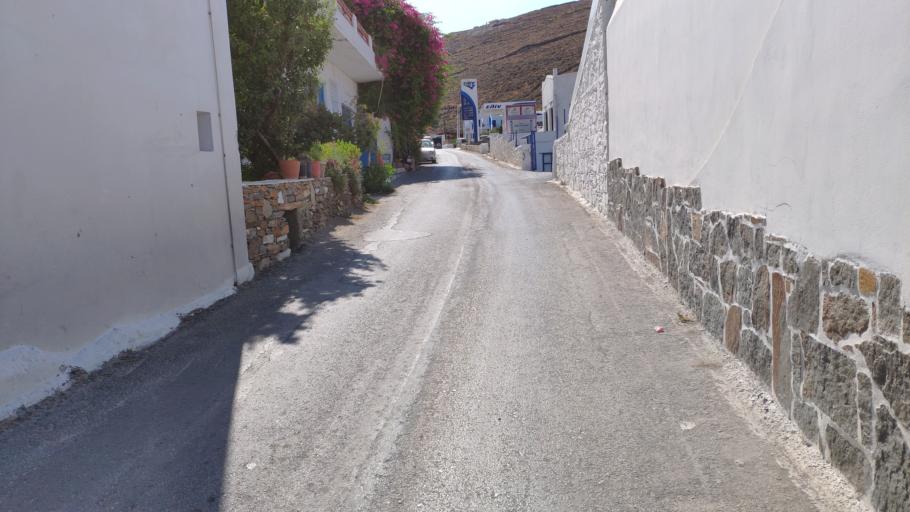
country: GR
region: South Aegean
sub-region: Nomos Kykladon
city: Kythnos
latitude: 37.3891
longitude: 24.3982
